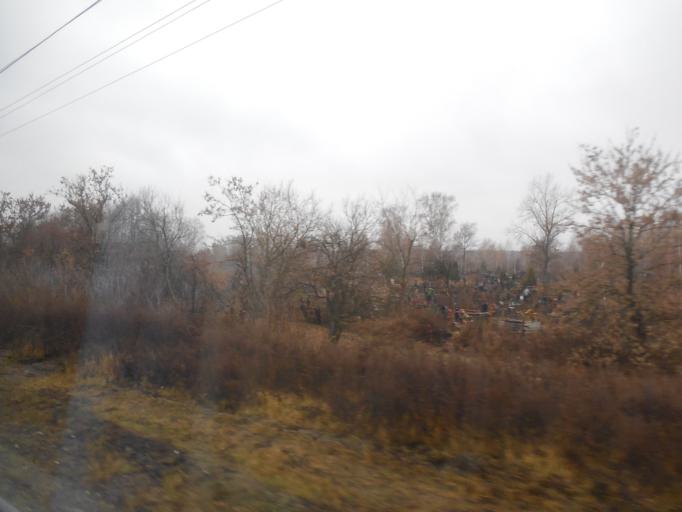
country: RU
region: Moskovskaya
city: Vidnoye
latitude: 55.5326
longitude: 37.6980
